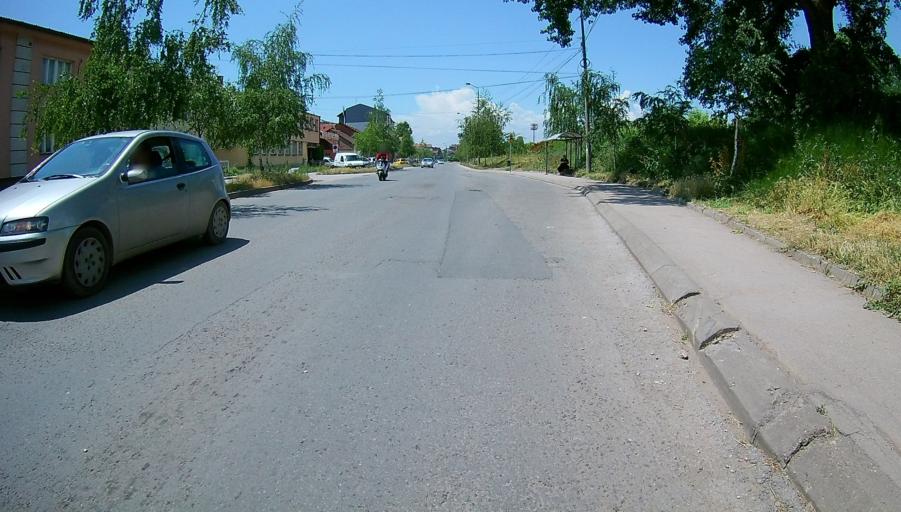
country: RS
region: Central Serbia
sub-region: Nisavski Okrug
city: Nis
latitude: 43.3119
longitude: 21.9100
